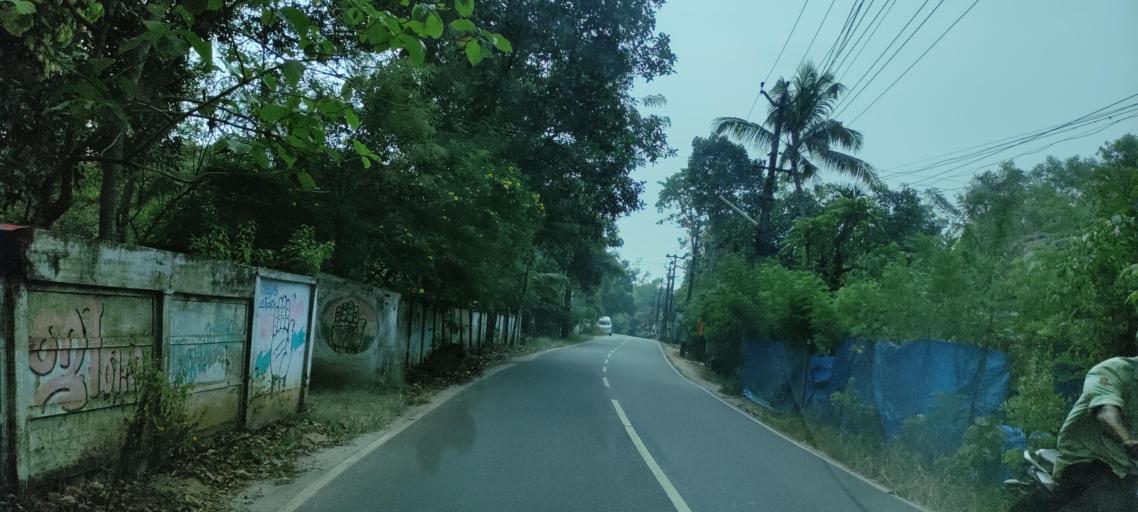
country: IN
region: Kerala
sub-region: Alappuzha
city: Alleppey
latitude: 9.5643
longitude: 76.3349
